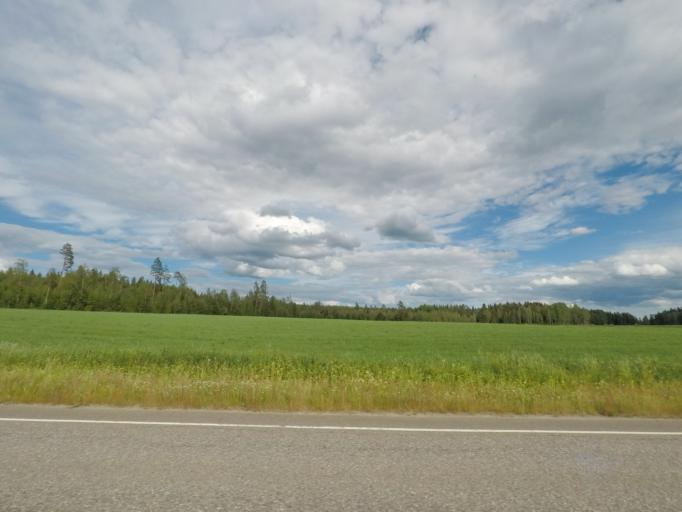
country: FI
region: Paijanne Tavastia
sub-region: Lahti
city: Hollola
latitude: 60.8250
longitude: 25.4879
